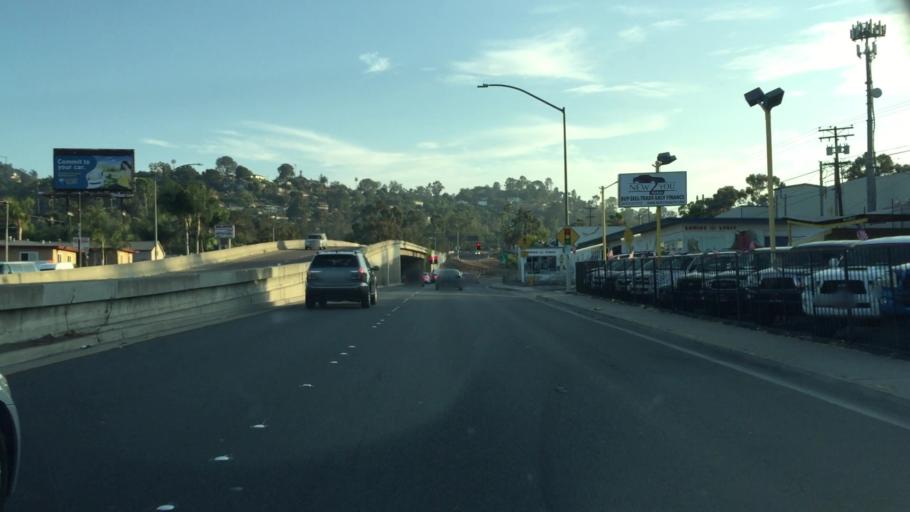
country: US
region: California
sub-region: San Diego County
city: El Cajon
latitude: 32.7843
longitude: -116.9783
